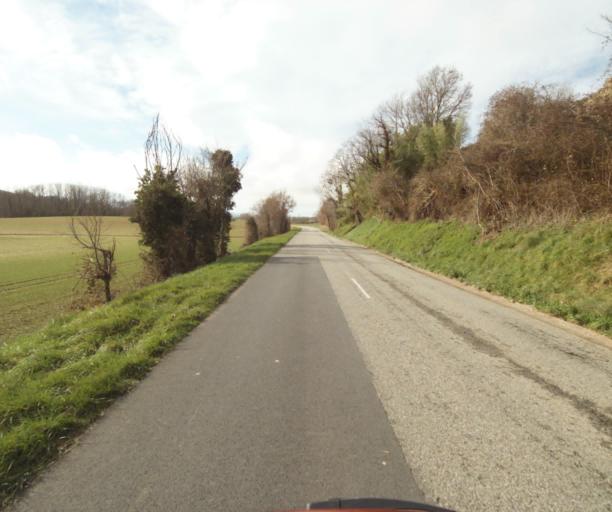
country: FR
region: Midi-Pyrenees
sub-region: Departement de l'Ariege
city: Pamiers
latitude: 43.1397
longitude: 1.5647
